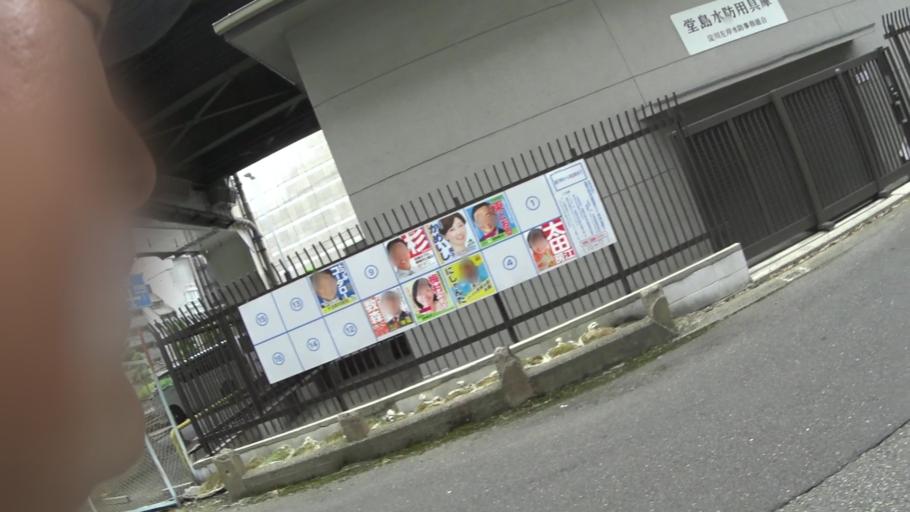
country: JP
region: Osaka
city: Osaka-shi
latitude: 34.6957
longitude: 135.4920
